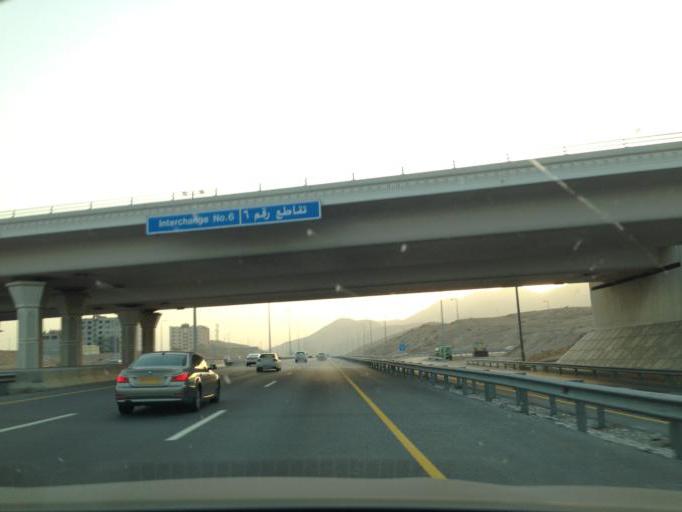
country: OM
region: Muhafazat Masqat
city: Bawshar
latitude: 23.5692
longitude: 58.4068
